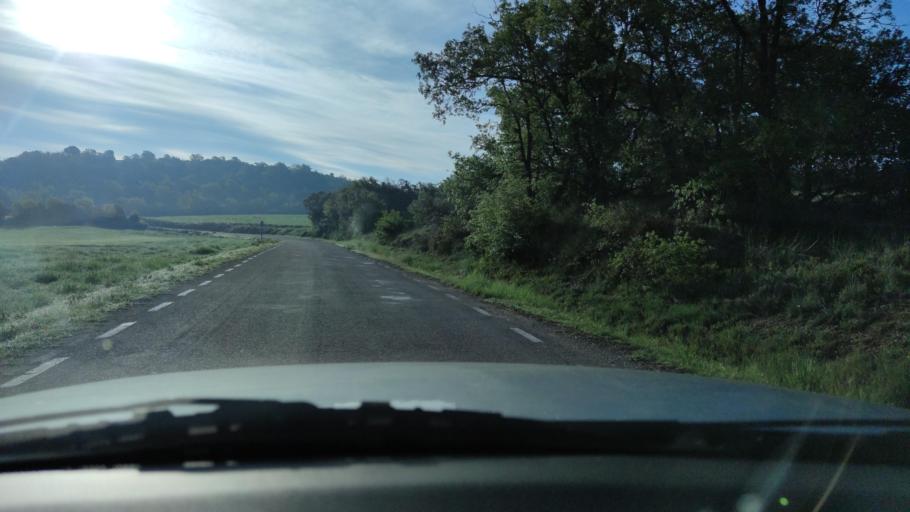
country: ES
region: Catalonia
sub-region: Provincia de Lleida
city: Artesa de Segre
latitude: 41.8612
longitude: 1.0702
